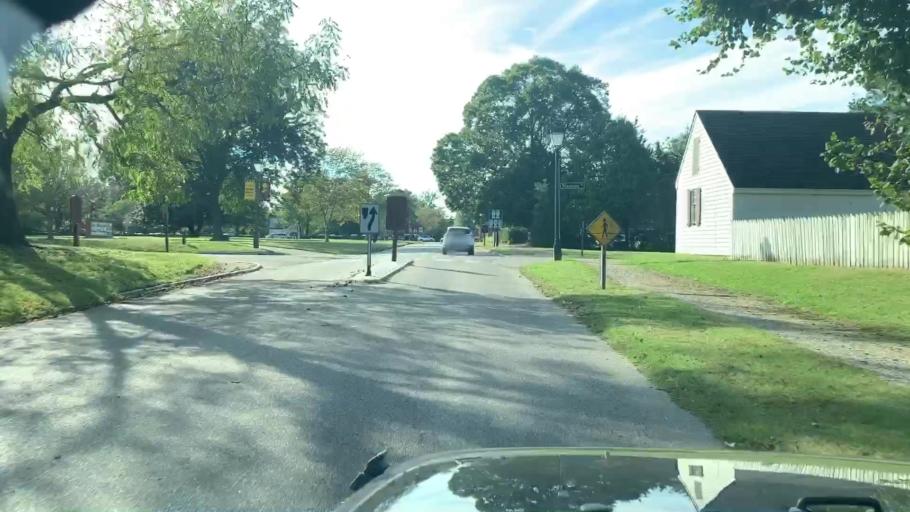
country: US
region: Virginia
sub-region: City of Williamsburg
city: Williamsburg
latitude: 37.2698
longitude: -76.7034
